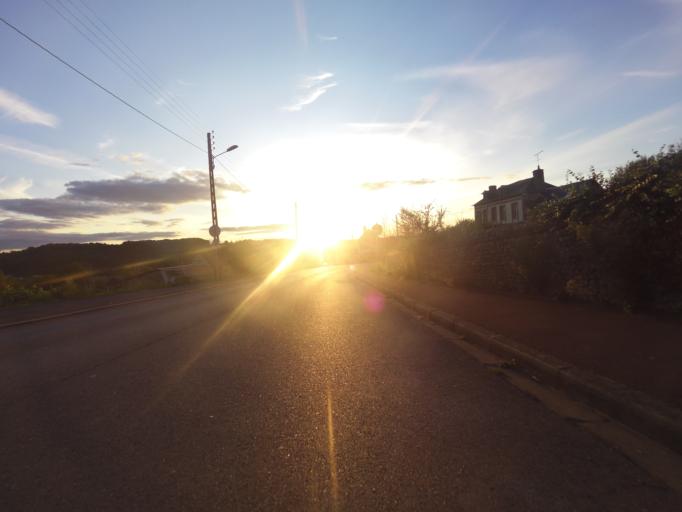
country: FR
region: Lower Normandy
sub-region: Departement du Calvados
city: La Vespiere
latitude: 49.0235
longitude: 0.4116
